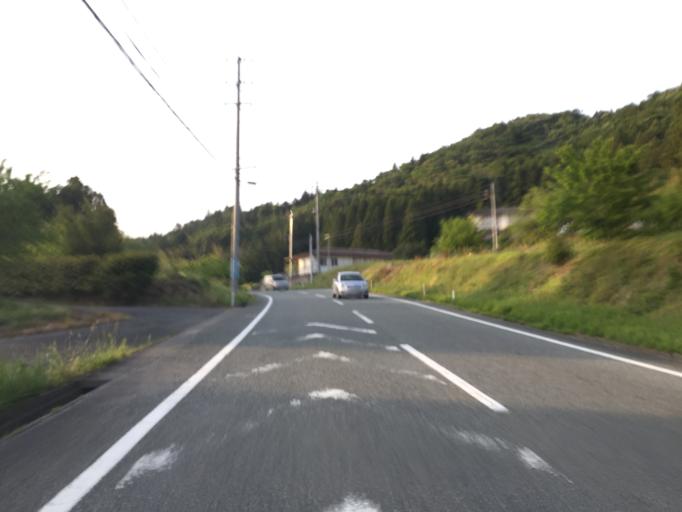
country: JP
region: Fukushima
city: Iwaki
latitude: 37.2380
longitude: 140.9775
